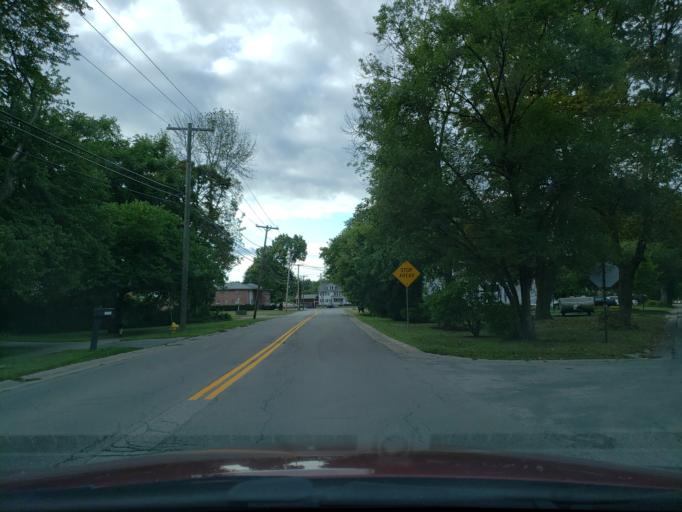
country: US
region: New York
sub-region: Monroe County
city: Greece
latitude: 43.2163
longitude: -77.6526
